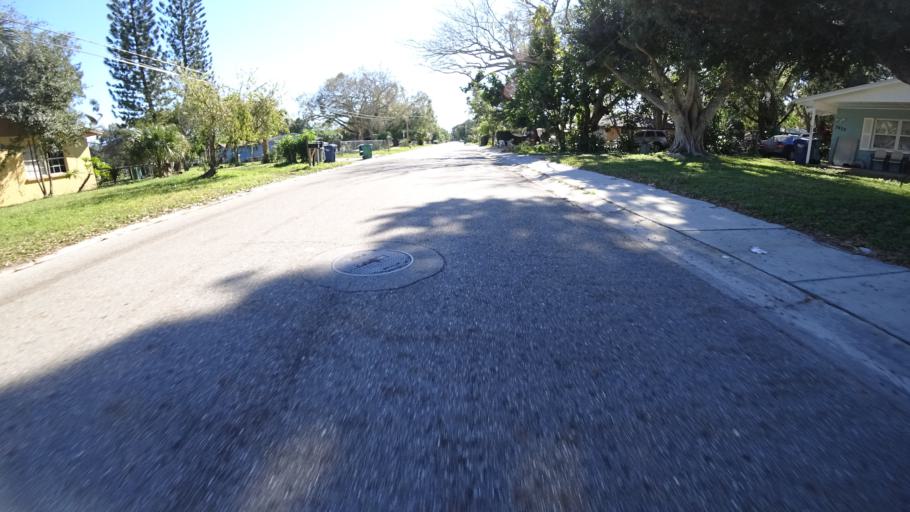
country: US
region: Florida
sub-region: Manatee County
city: Whitfield
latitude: 27.4369
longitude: -82.5524
